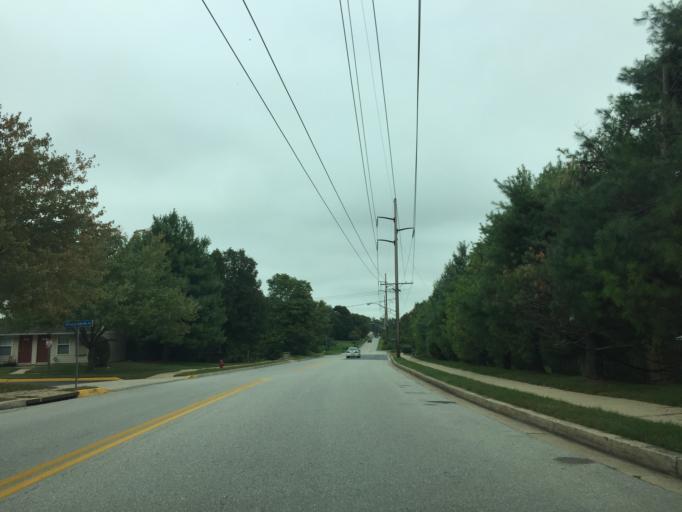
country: US
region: Maryland
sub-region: Baltimore County
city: Middle River
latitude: 39.3372
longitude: -76.4388
